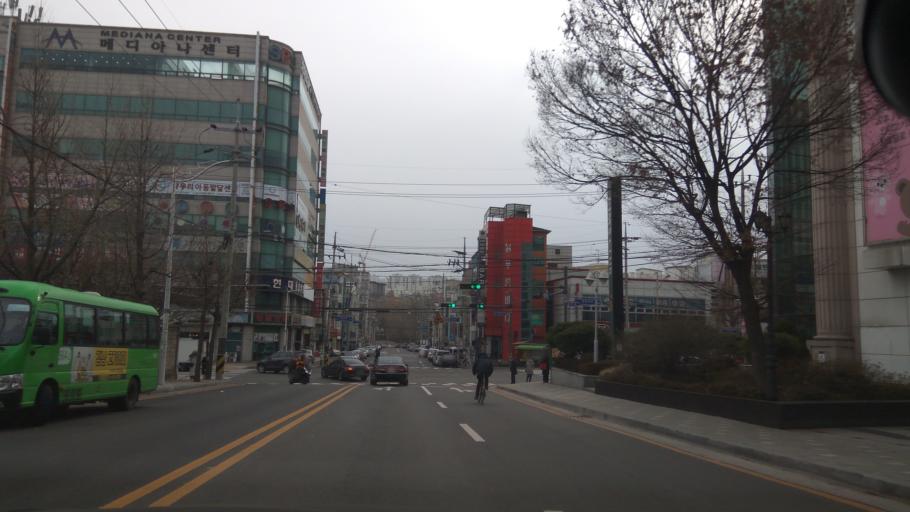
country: KR
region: Incheon
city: Incheon
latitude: 37.4909
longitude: 126.7110
